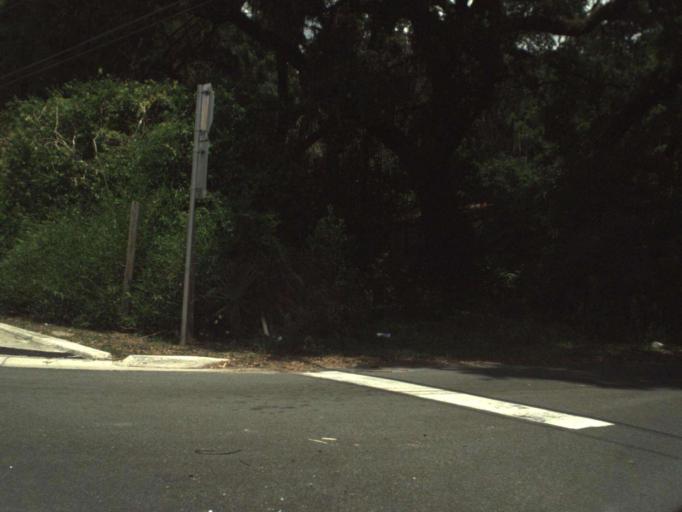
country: US
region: Florida
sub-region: Sumter County
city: Wildwood
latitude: 28.9346
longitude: -82.0370
